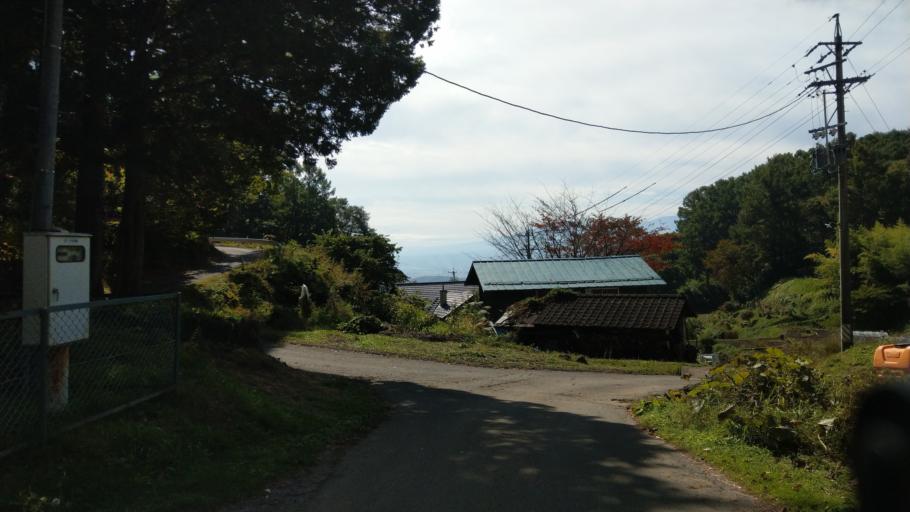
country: JP
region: Nagano
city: Komoro
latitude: 36.3584
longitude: 138.4316
